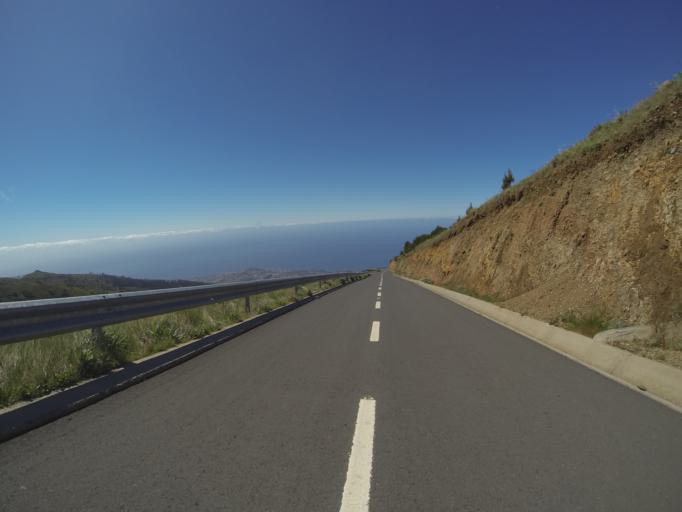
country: PT
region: Madeira
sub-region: Camara de Lobos
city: Curral das Freiras
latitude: 32.7130
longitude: -16.9541
